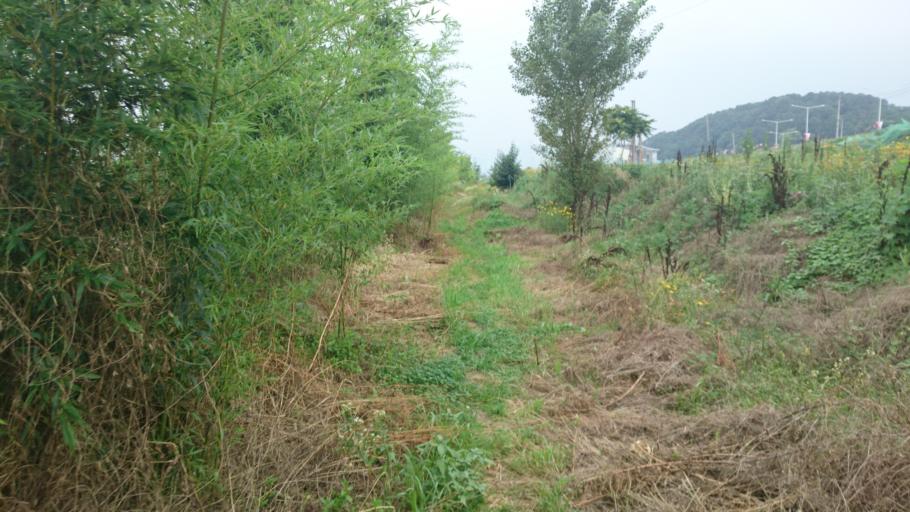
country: KR
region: Daegu
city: Hwawon
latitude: 35.8519
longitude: 128.4700
